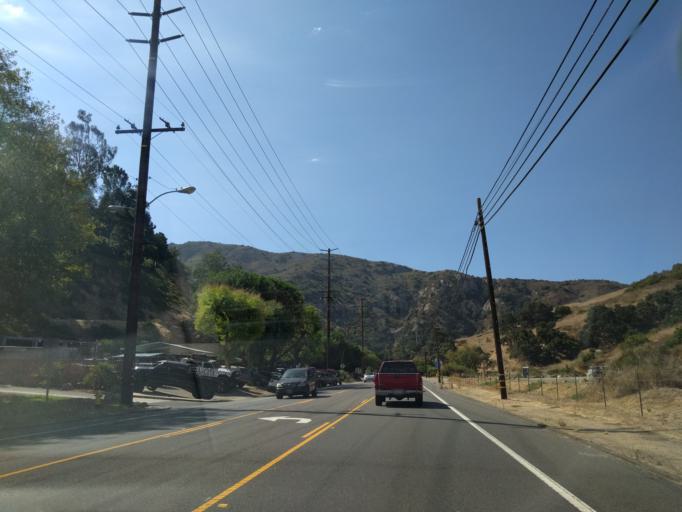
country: US
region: California
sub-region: Orange County
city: Laguna Beach
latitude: 33.5677
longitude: -117.7638
